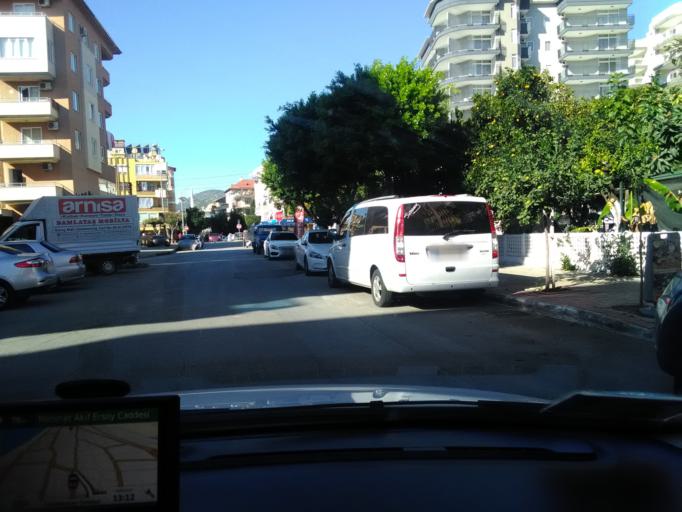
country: TR
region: Antalya
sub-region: Alanya
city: Alanya
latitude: 36.5509
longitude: 31.9869
